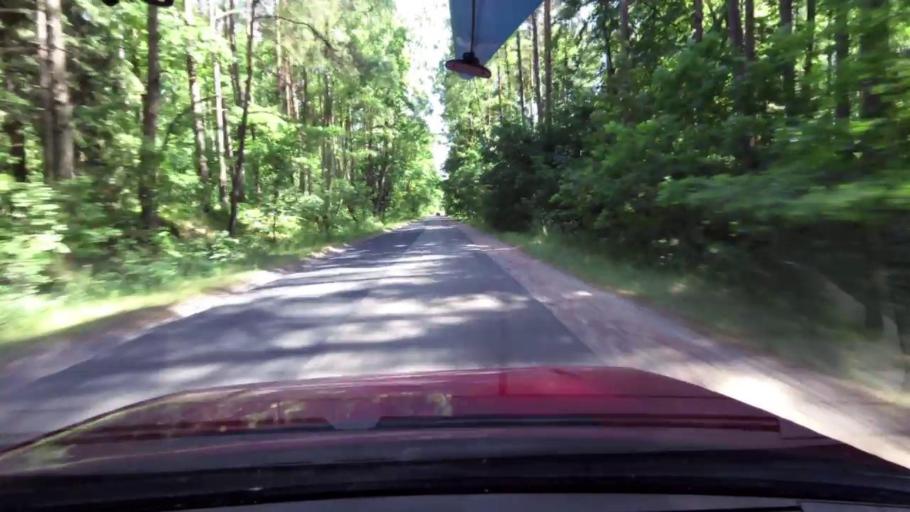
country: PL
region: Pomeranian Voivodeship
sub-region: Powiat slupski
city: Kobylnica
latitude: 54.3321
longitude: 16.9596
